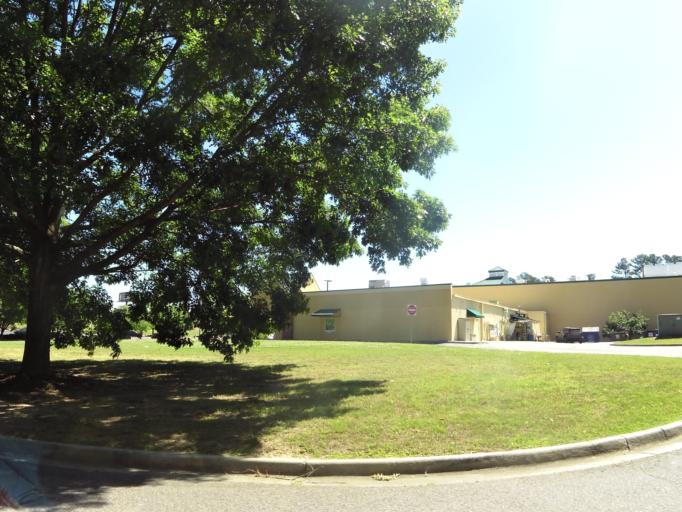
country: US
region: Georgia
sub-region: Columbia County
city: Martinez
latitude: 33.5081
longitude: -82.0324
